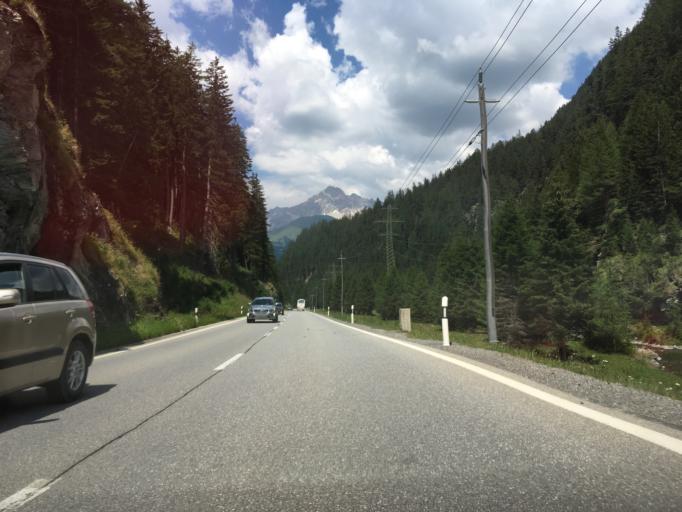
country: CH
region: Grisons
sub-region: Albula District
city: Tiefencastel
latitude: 46.5382
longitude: 9.6244
